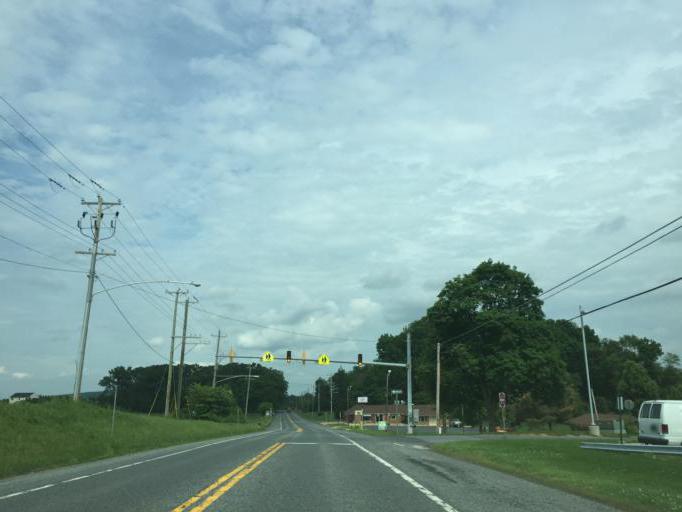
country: US
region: Pennsylvania
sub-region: York County
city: Susquehanna Trails
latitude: 39.6766
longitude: -76.4003
